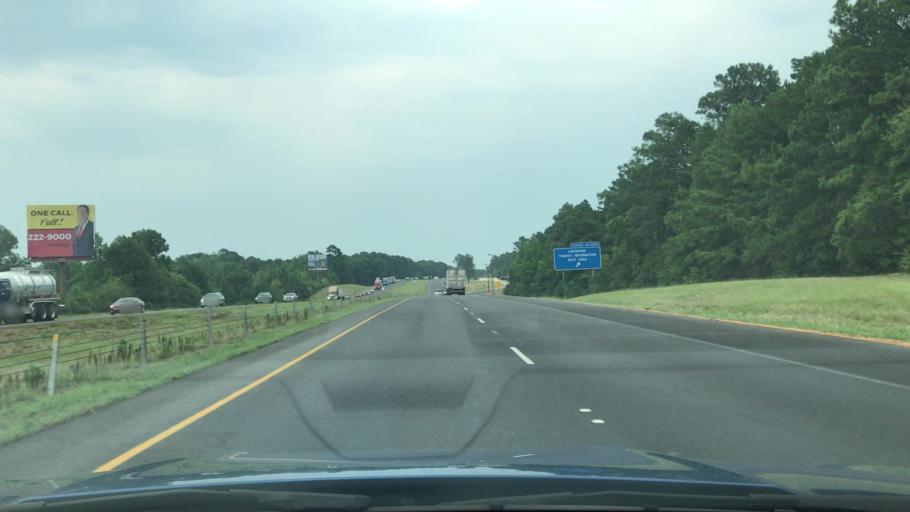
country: US
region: Louisiana
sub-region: Caddo Parish
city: Greenwood
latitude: 32.4516
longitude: -94.0084
